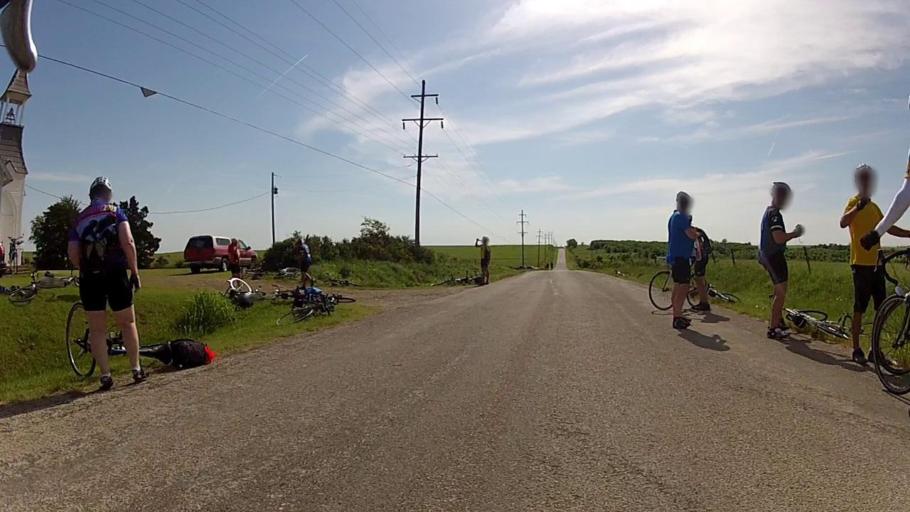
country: US
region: Kansas
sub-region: Cowley County
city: Winfield
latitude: 37.0709
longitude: -96.6811
